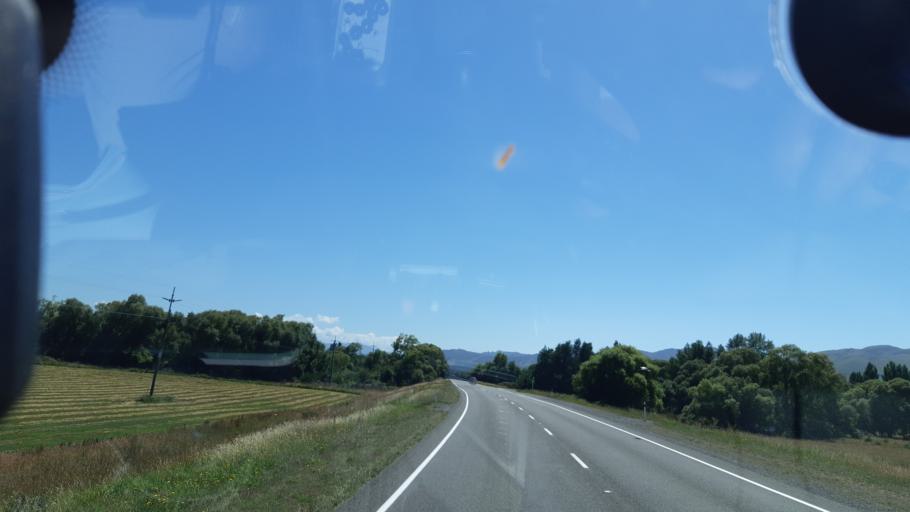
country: NZ
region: Canterbury
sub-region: Kaikoura District
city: Kaikoura
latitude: -42.7264
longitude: 173.2797
